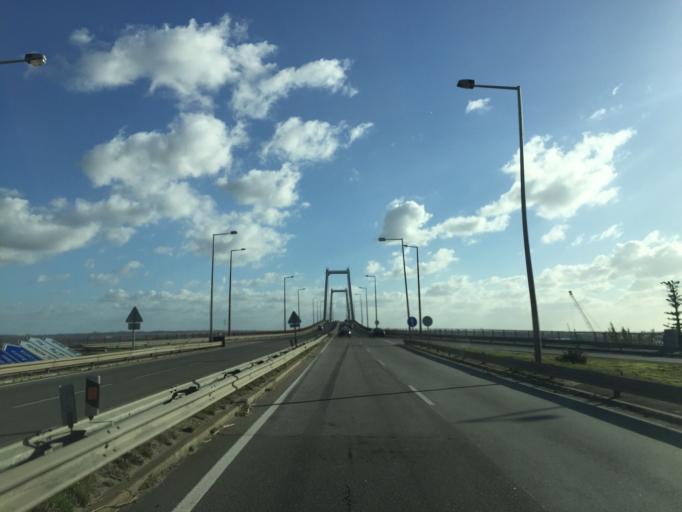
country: PT
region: Coimbra
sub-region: Figueira da Foz
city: Figueira da Foz
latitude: 40.1507
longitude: -8.8418
